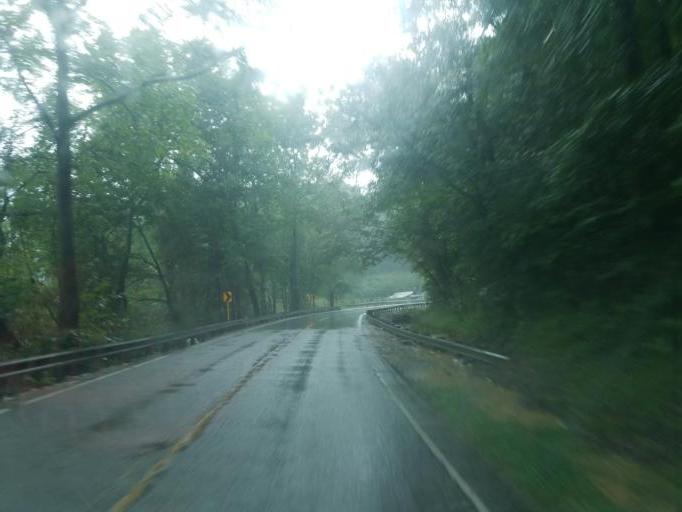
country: US
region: Kentucky
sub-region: Rowan County
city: Morehead
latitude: 38.2639
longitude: -83.3332
